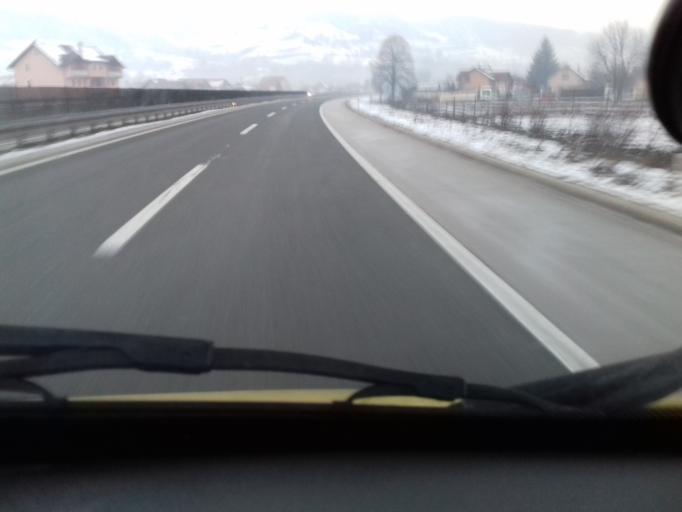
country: BA
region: Federation of Bosnia and Herzegovina
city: Ilijas
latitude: 43.9441
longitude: 18.2595
